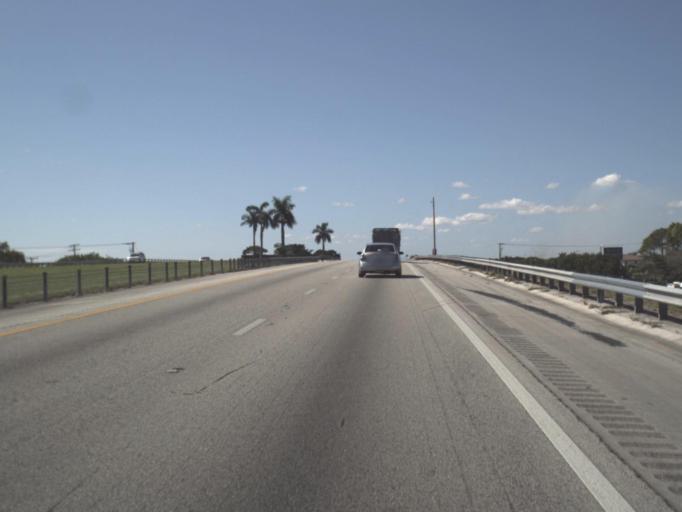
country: US
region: Florida
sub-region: Miami-Dade County
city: Naranja
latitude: 25.5198
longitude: -80.4036
